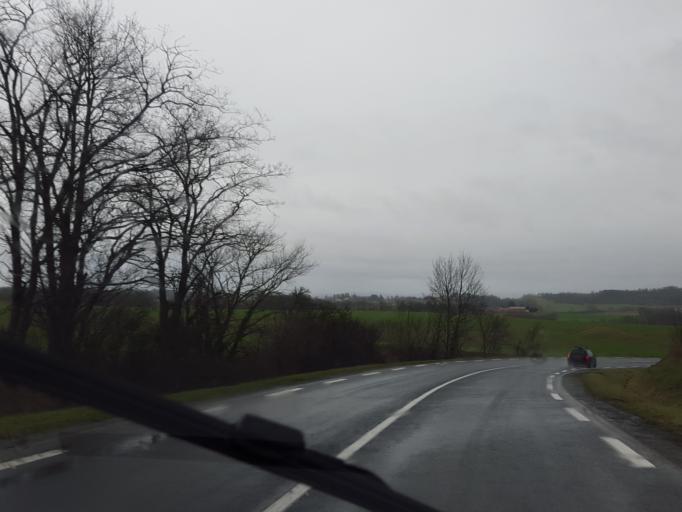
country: FR
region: Midi-Pyrenees
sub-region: Departement de l'Ariege
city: Mirepoix
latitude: 43.1483
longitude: 1.9612
